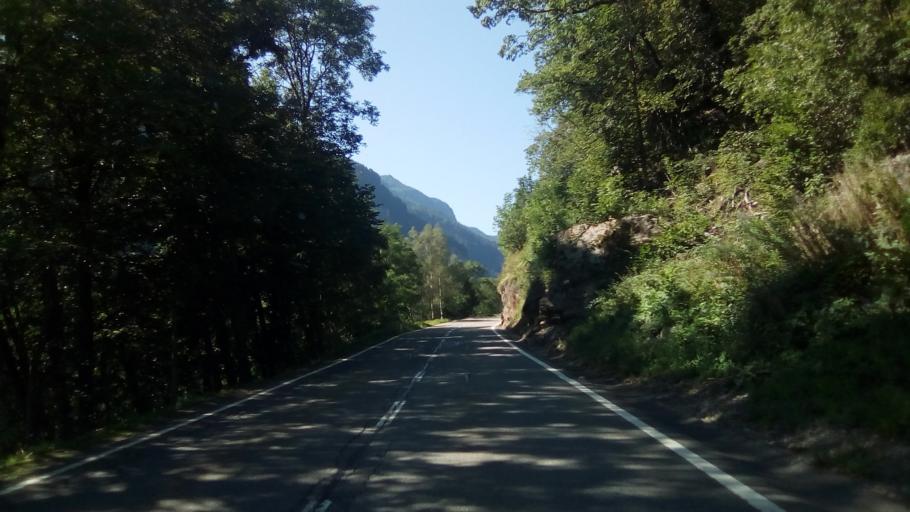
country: CH
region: Valais
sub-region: Saint-Maurice District
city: Salvan
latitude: 46.1207
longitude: 7.0291
